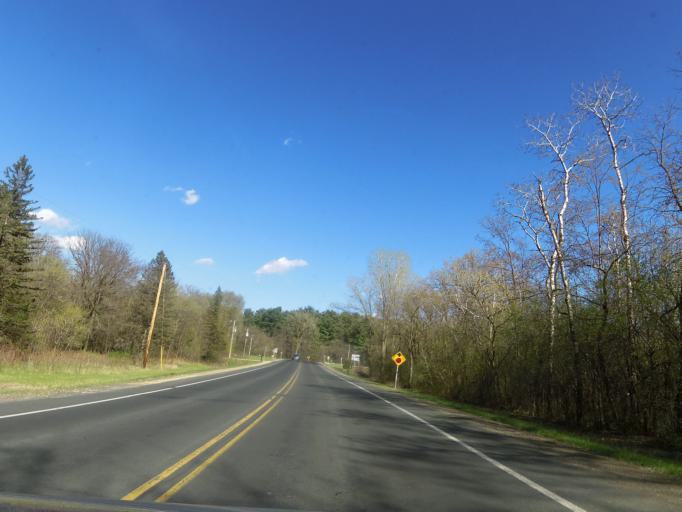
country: US
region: Wisconsin
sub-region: Saint Croix County
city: Somerset
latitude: 45.0259
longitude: -92.6582
